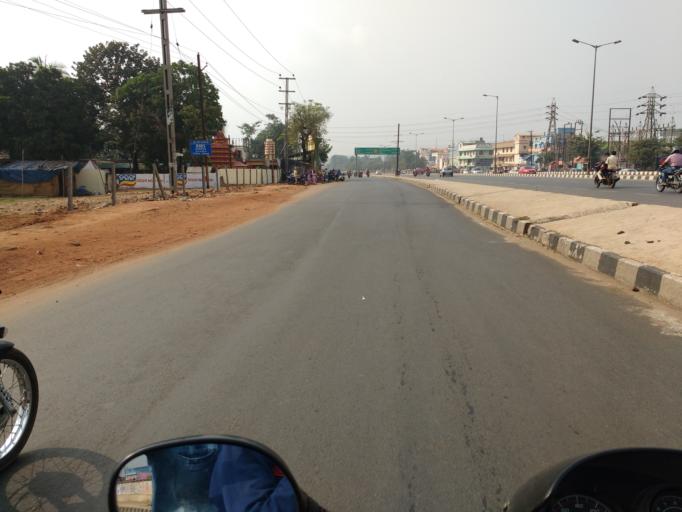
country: IN
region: Odisha
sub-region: Khordha
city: Bhubaneshwar
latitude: 20.2771
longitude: 85.7965
